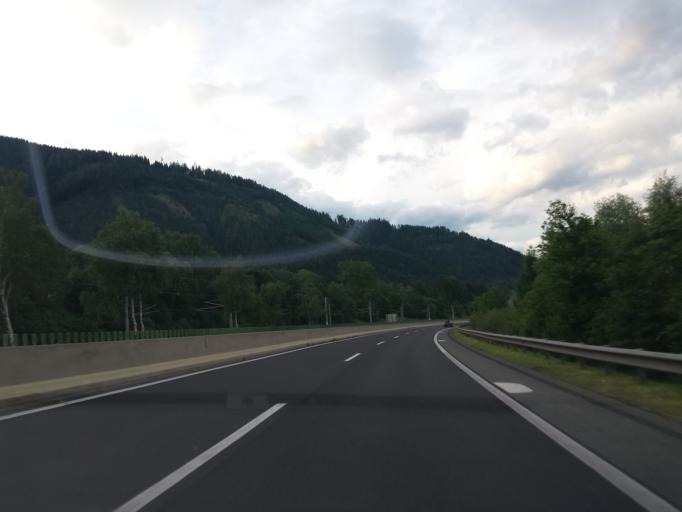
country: AT
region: Styria
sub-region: Politischer Bezirk Leoben
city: Kraubath an der Mur
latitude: 47.3135
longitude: 14.9523
